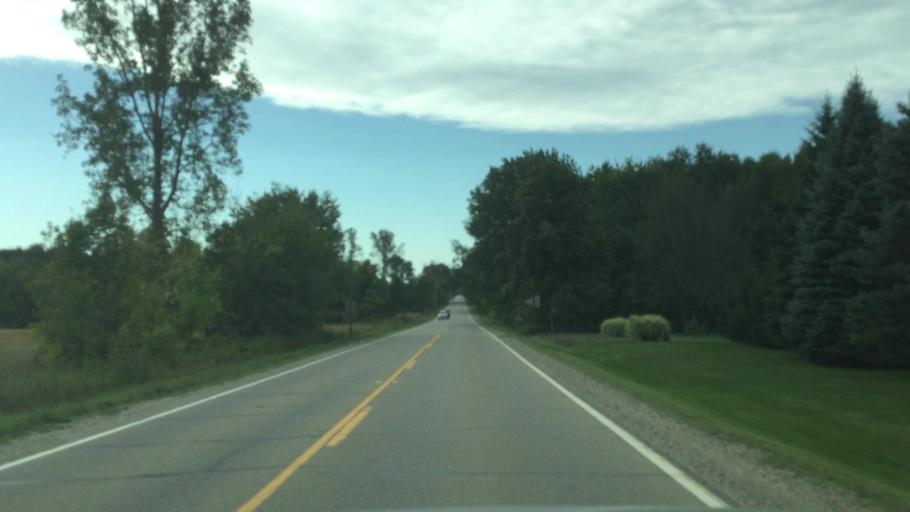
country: US
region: Michigan
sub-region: Livingston County
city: Howell
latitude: 42.6513
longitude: -83.8762
